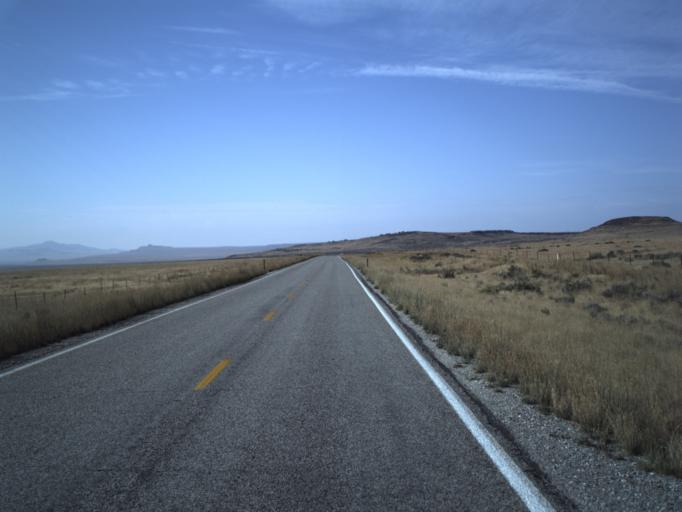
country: US
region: Idaho
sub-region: Minidoka County
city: Rupert
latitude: 41.8585
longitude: -113.1299
